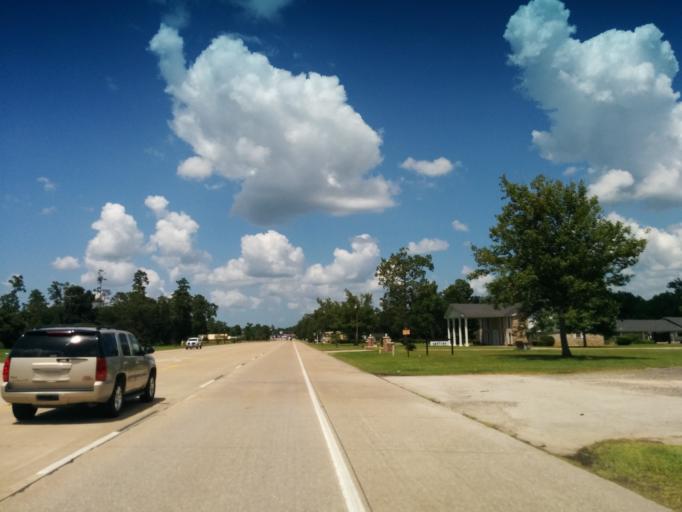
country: US
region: Texas
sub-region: Jasper County
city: Buna
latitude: 30.4351
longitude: -93.9746
